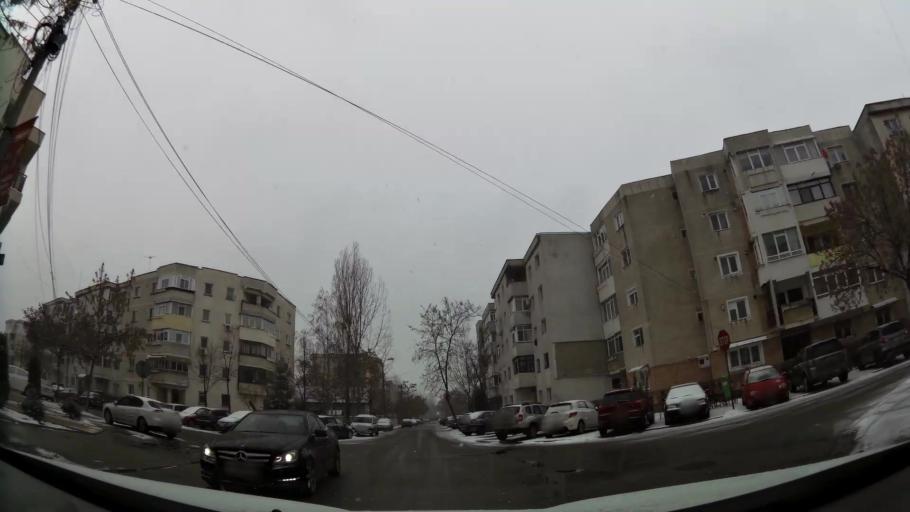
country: RO
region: Prahova
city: Ploiesti
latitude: 44.9369
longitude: 25.9974
